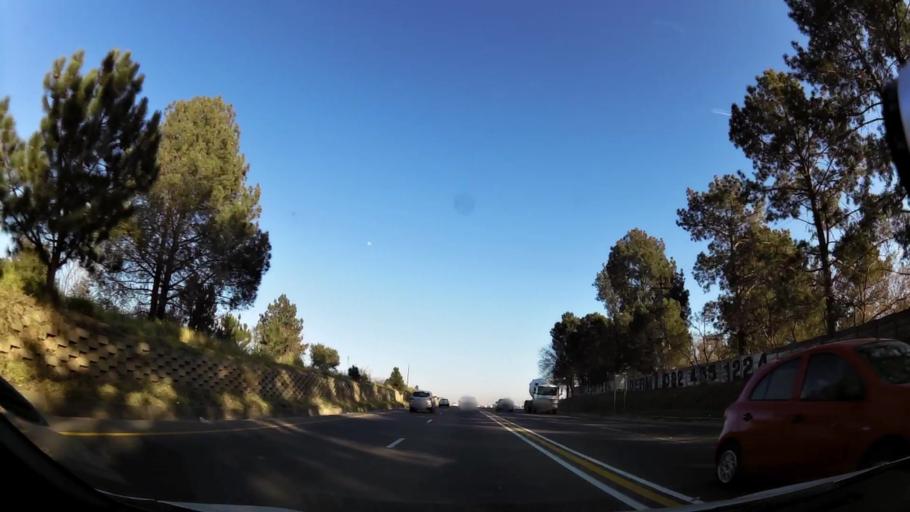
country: ZA
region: Gauteng
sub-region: City of Johannesburg Metropolitan Municipality
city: Midrand
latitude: -25.9407
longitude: 28.0985
